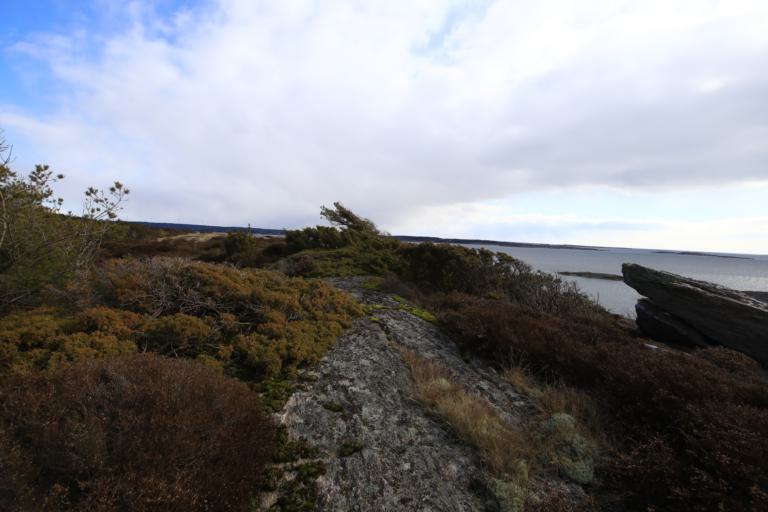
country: SE
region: Halland
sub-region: Kungsbacka Kommun
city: Frillesas
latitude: 57.2151
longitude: 12.1417
